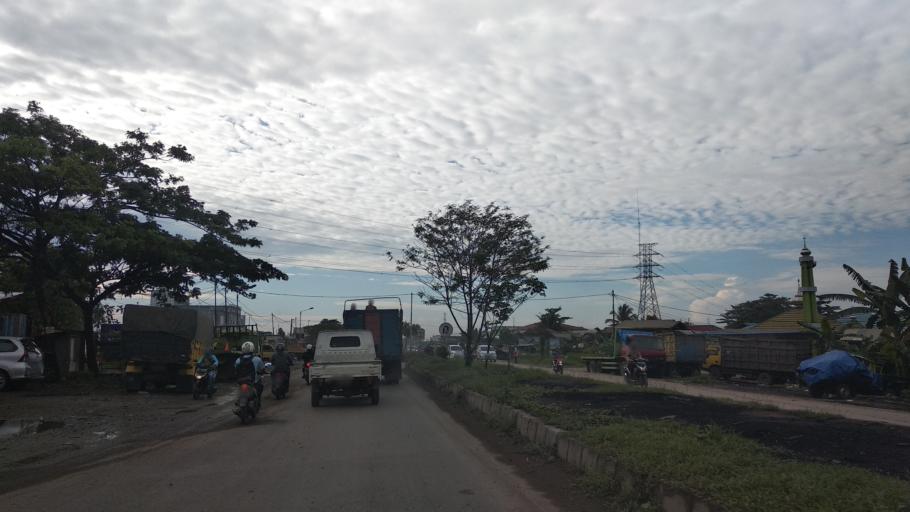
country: ID
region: South Kalimantan
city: Banjarmasin
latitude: -3.3344
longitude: 114.5651
